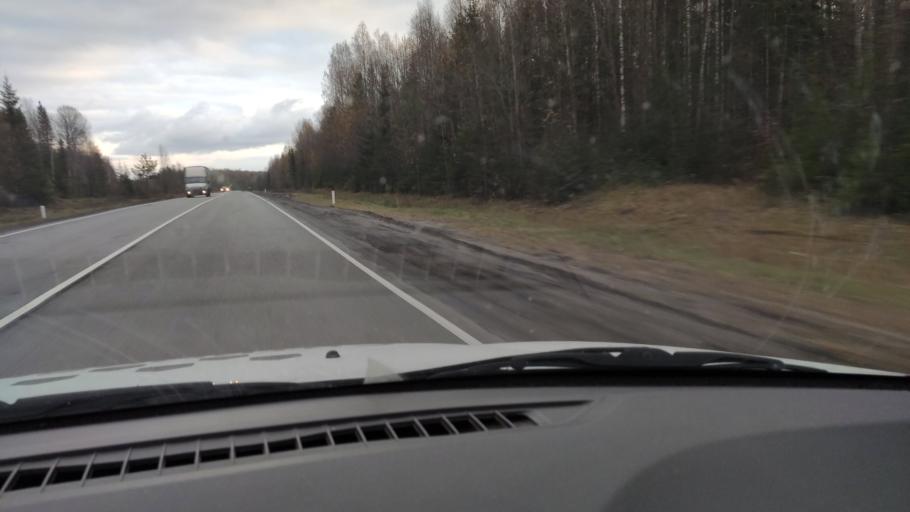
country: RU
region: Kirov
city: Omutninsk
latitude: 58.7536
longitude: 52.0472
